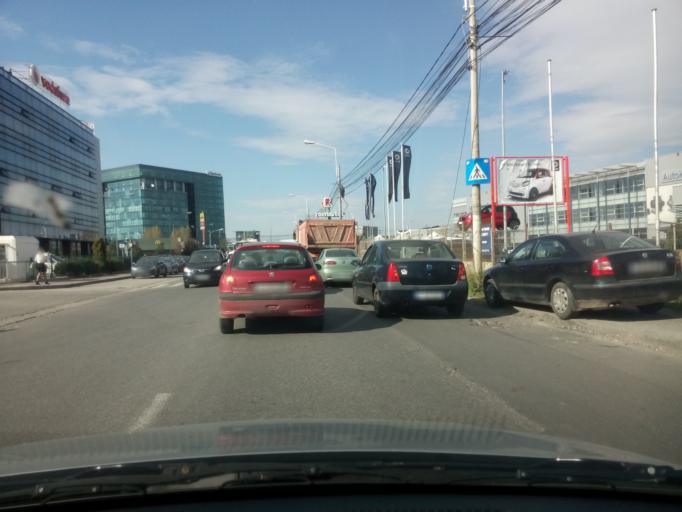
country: RO
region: Ilfov
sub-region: Voluntari City
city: Voluntari
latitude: 44.4905
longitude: 26.1265
